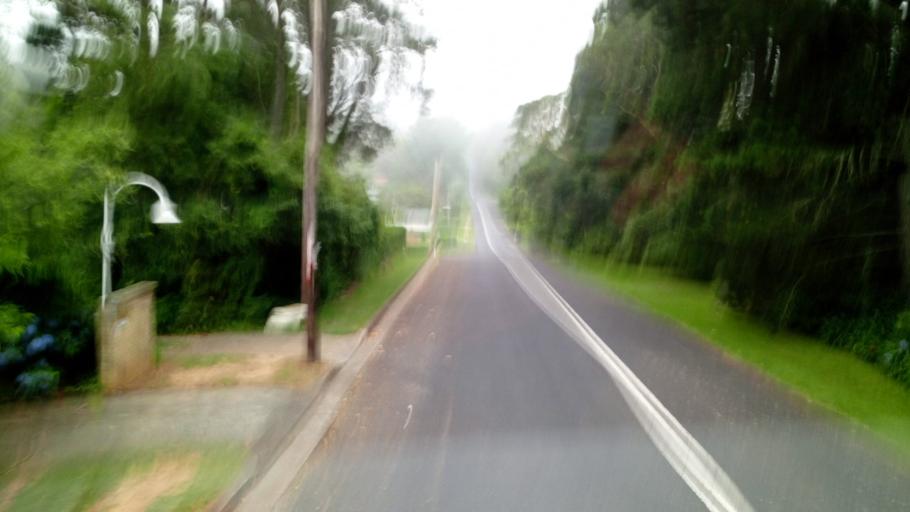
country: AU
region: New South Wales
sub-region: Blue Mountains Municipality
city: Leura
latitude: -33.7203
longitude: 150.3387
